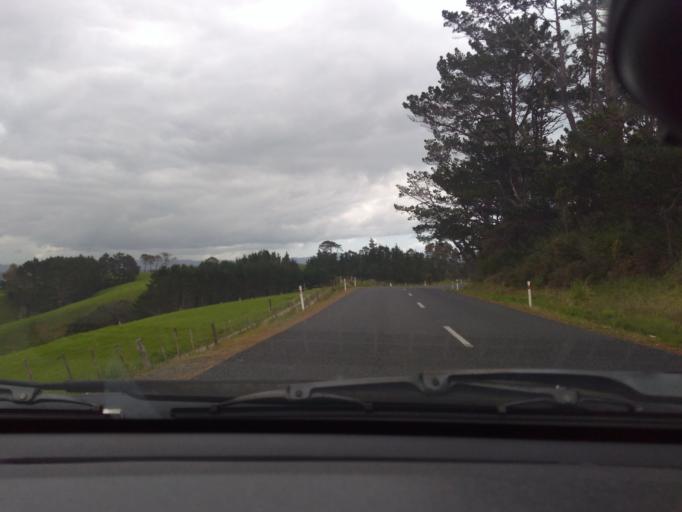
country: NZ
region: Auckland
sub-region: Auckland
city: Warkworth
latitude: -36.4495
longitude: 174.7559
